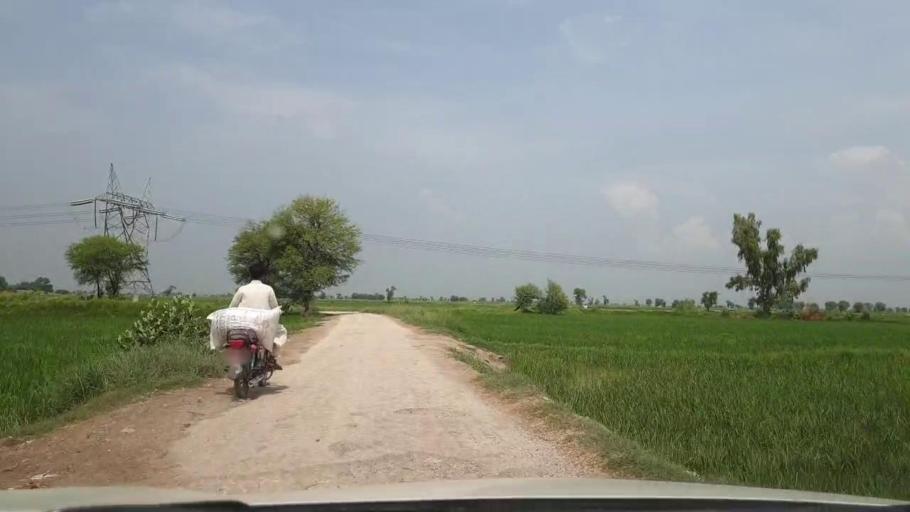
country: PK
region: Sindh
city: Dokri
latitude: 27.3901
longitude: 68.0556
